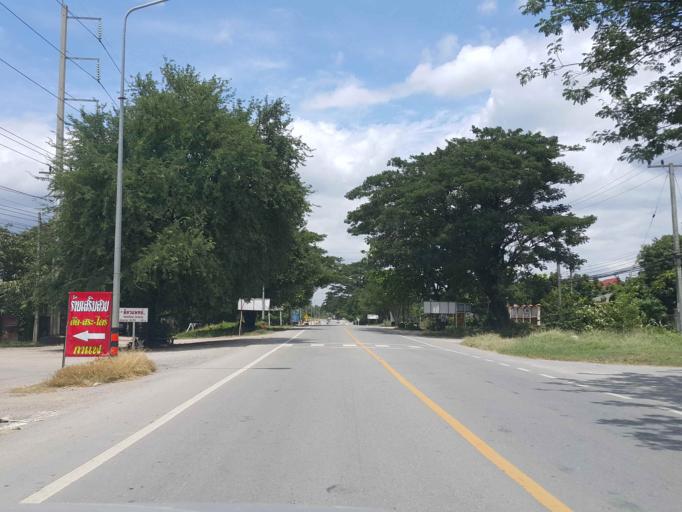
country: TH
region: Lamphun
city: Ban Hong
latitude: 18.3313
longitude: 98.8175
